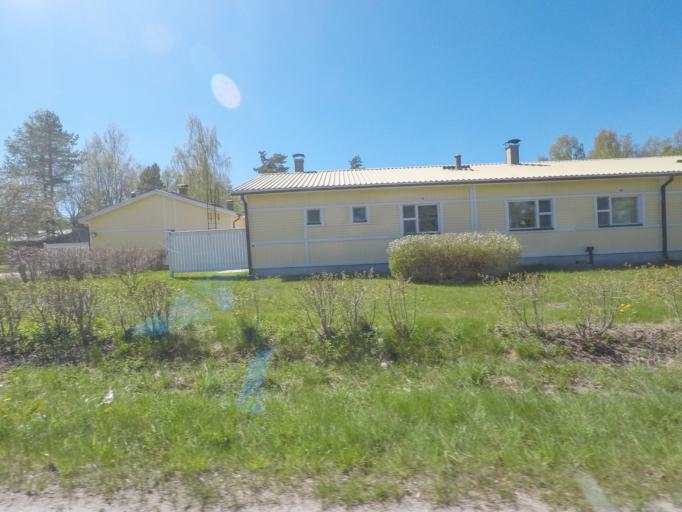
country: FI
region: Uusimaa
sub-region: Helsinki
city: Sammatti
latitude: 60.3233
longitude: 23.8173
